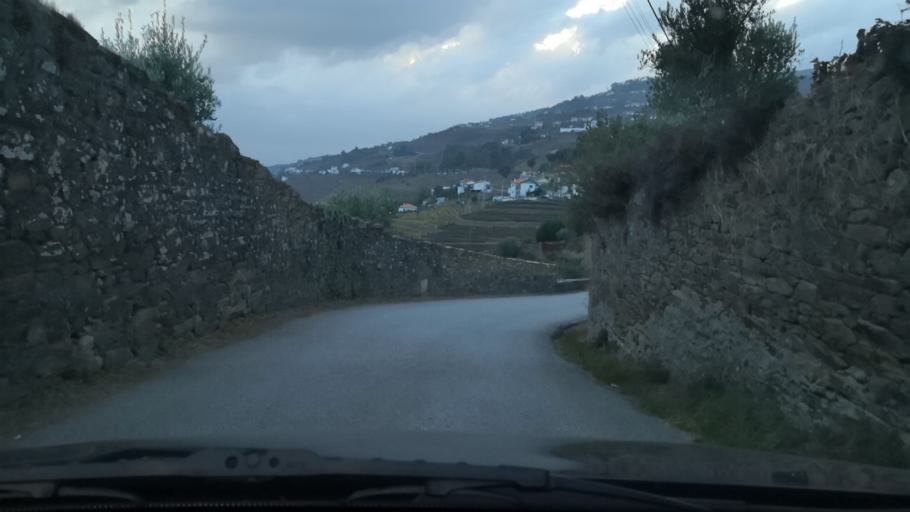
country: PT
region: Vila Real
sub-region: Mesao Frio
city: Mesao Frio
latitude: 41.1827
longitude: -7.8489
